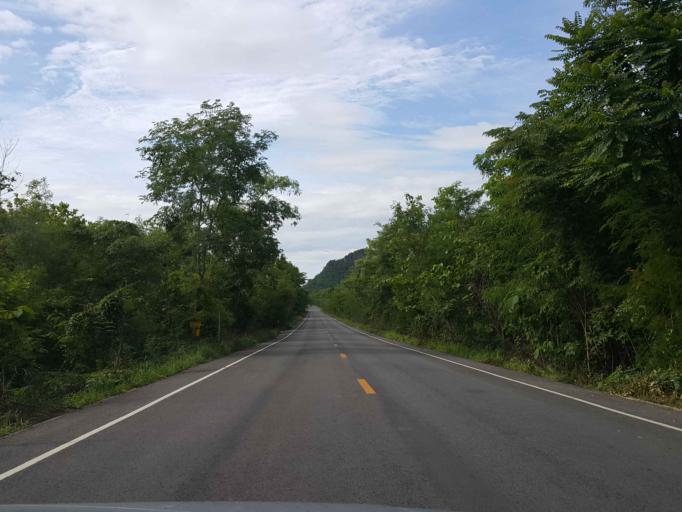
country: TH
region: Sukhothai
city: Thung Saliam
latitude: 17.2951
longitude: 99.5269
